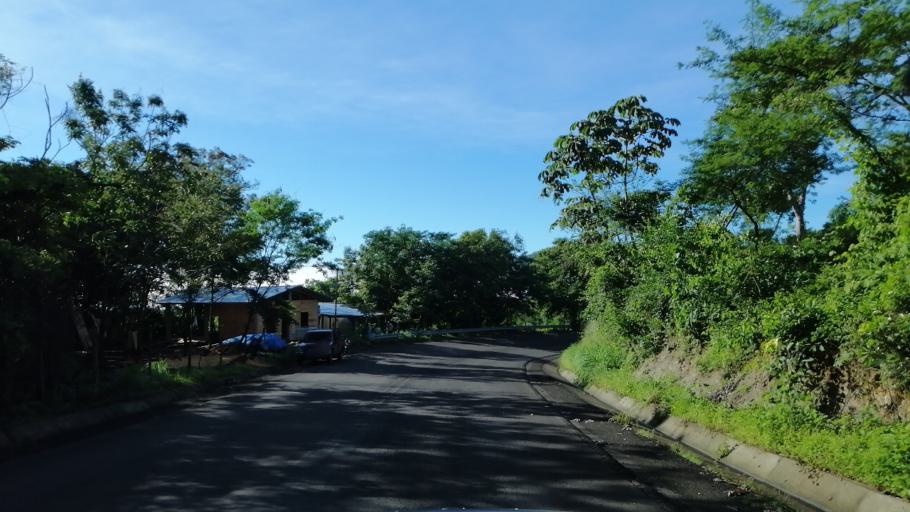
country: SV
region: Morazan
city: Cacaopera
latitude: 13.7818
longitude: -88.1032
